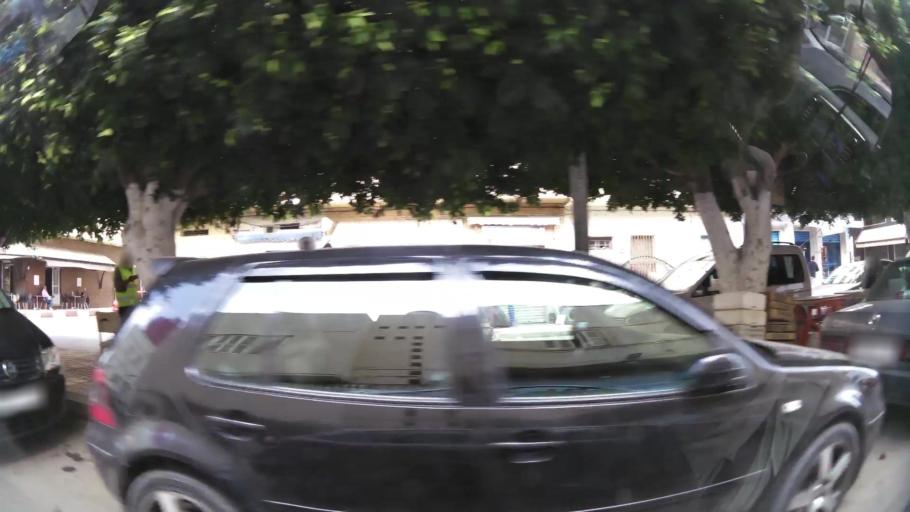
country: MA
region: Oriental
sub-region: Nador
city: Nador
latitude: 35.1787
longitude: -2.9239
